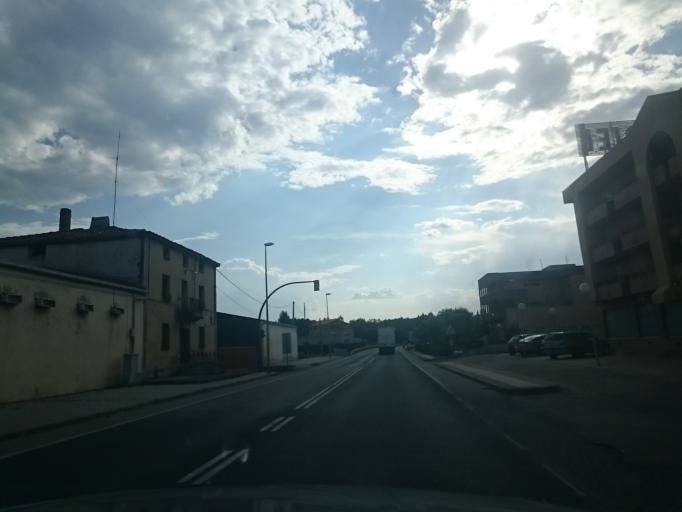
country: ES
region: Castille and Leon
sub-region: Provincia de Burgos
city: Belorado
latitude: 42.4178
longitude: -3.1985
